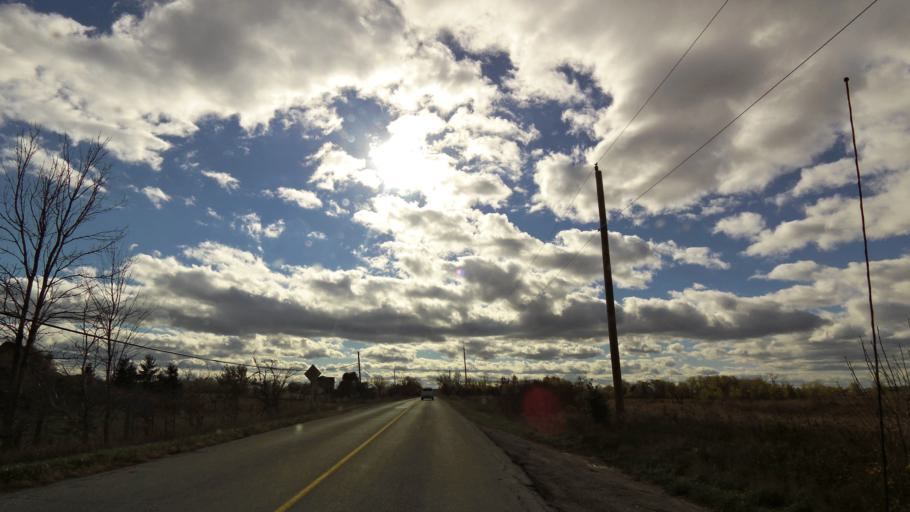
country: CA
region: Ontario
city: Burlington
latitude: 43.4658
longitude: -79.8092
